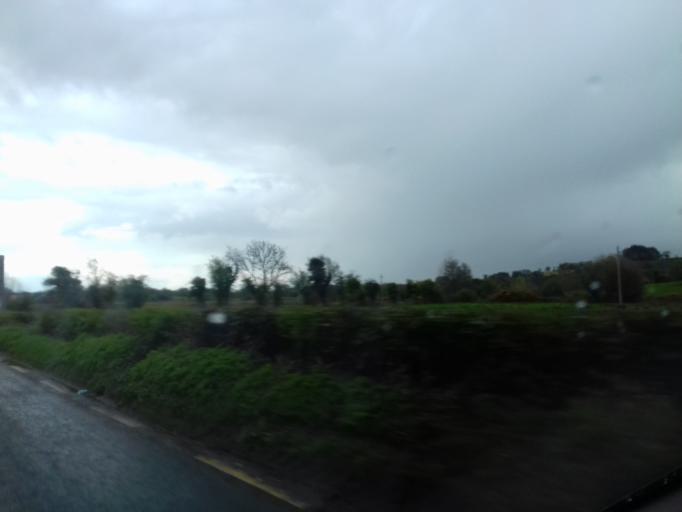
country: IE
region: Ulster
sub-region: An Cabhan
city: Ballyconnell
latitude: 54.1293
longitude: -7.6864
